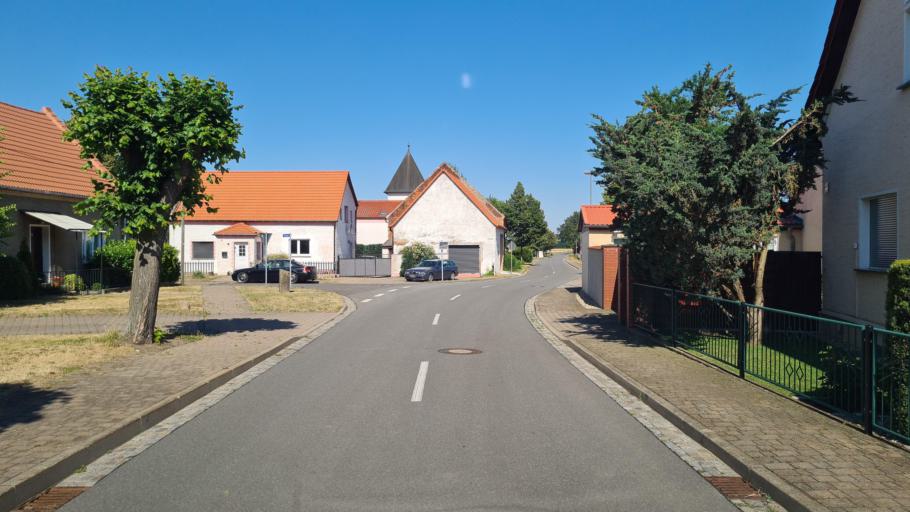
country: DE
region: Saxony-Anhalt
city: Prettin
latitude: 51.6936
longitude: 12.9189
